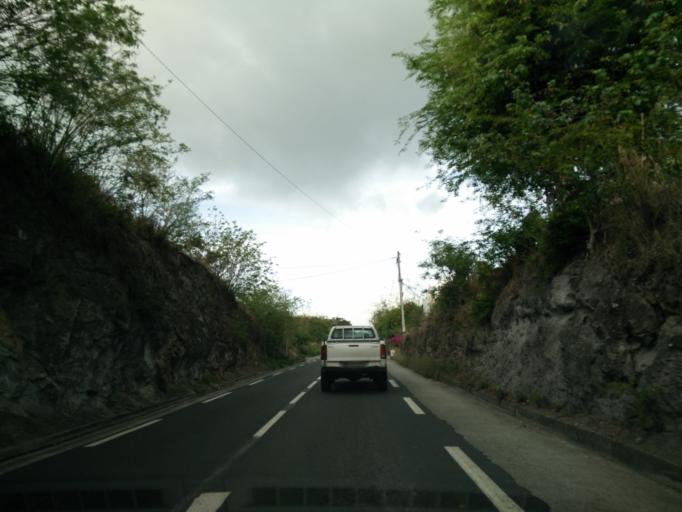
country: MQ
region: Martinique
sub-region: Martinique
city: Saint-Pierre
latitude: 14.6959
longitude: -61.1759
